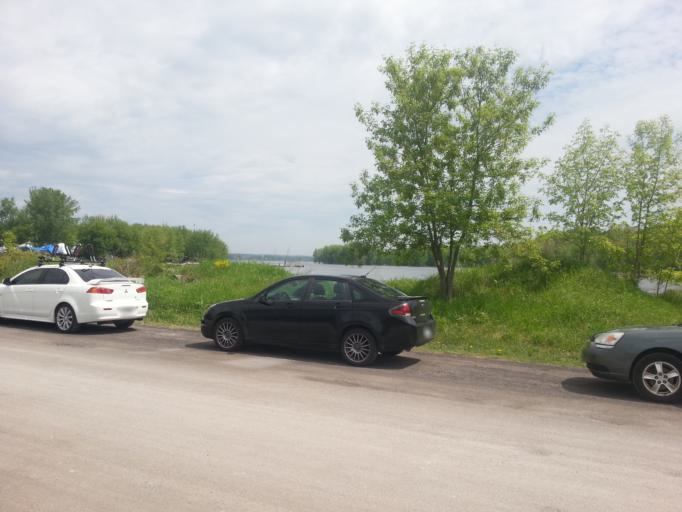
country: CA
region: Ontario
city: Clarence-Rockland
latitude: 45.4987
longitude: -75.4842
